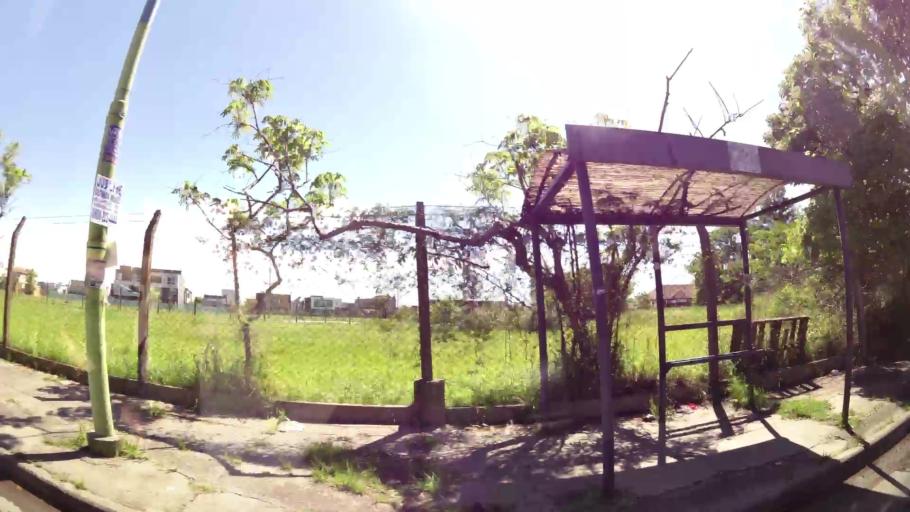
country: AR
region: Buenos Aires
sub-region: Partido de Quilmes
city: Quilmes
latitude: -34.7001
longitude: -58.2894
